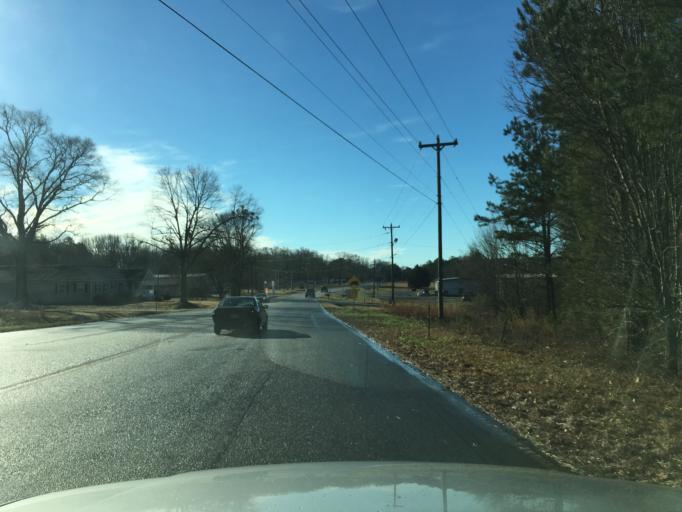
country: US
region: South Carolina
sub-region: Spartanburg County
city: Cowpens
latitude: 35.0156
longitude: -81.8727
